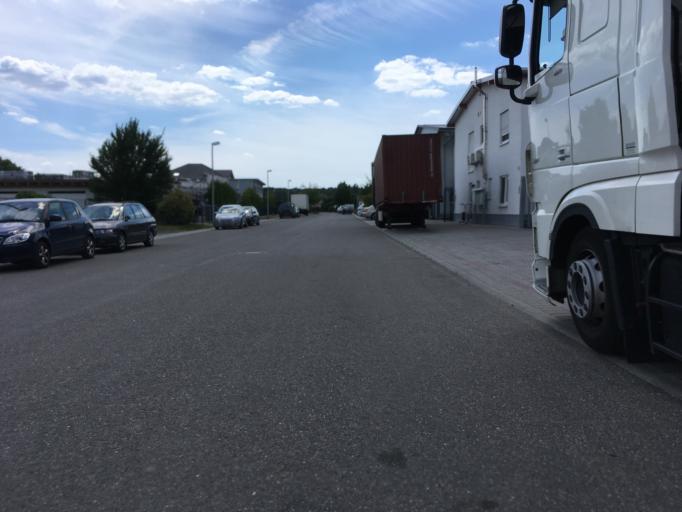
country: DE
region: Rheinland-Pfalz
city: Altrip
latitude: 49.4273
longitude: 8.4767
